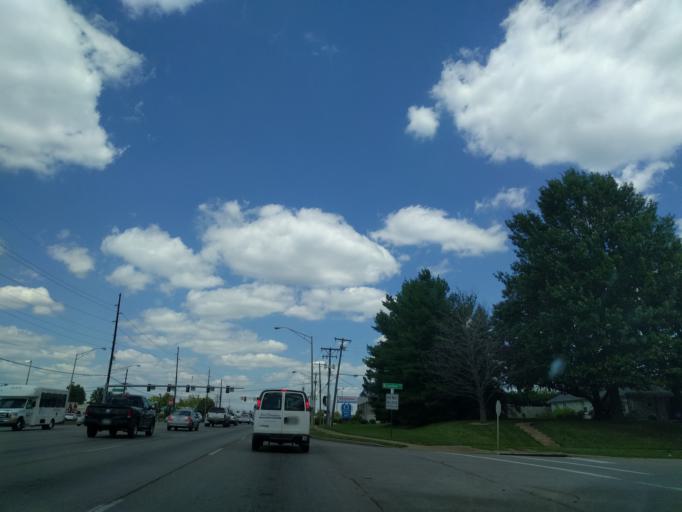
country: US
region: Kentucky
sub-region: Fayette County
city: Monticello
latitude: 37.9901
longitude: -84.5241
